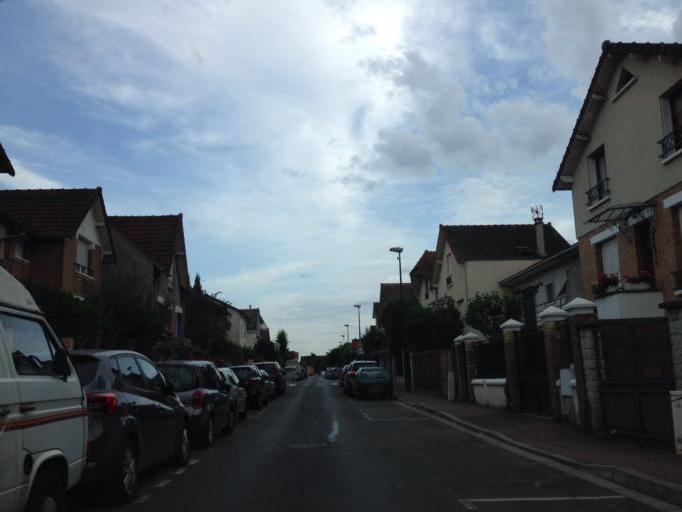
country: FR
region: Ile-de-France
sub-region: Departement des Hauts-de-Seine
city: Clamart
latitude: 48.7934
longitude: 2.2589
